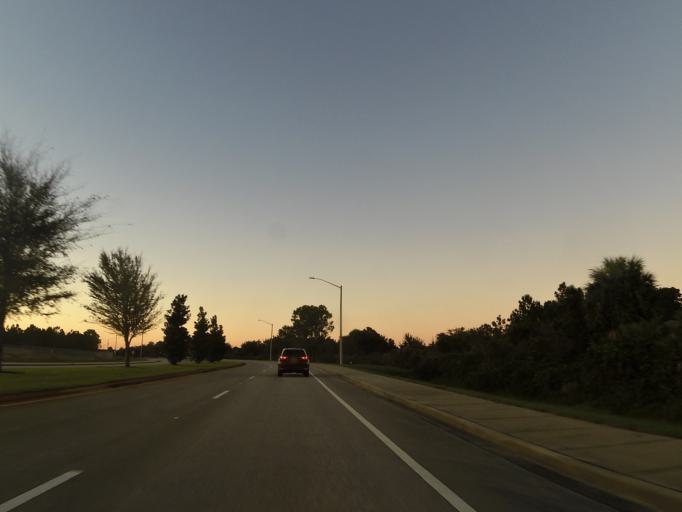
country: US
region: Florida
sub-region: Flagler County
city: Palm Coast
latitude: 29.5839
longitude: -81.2565
